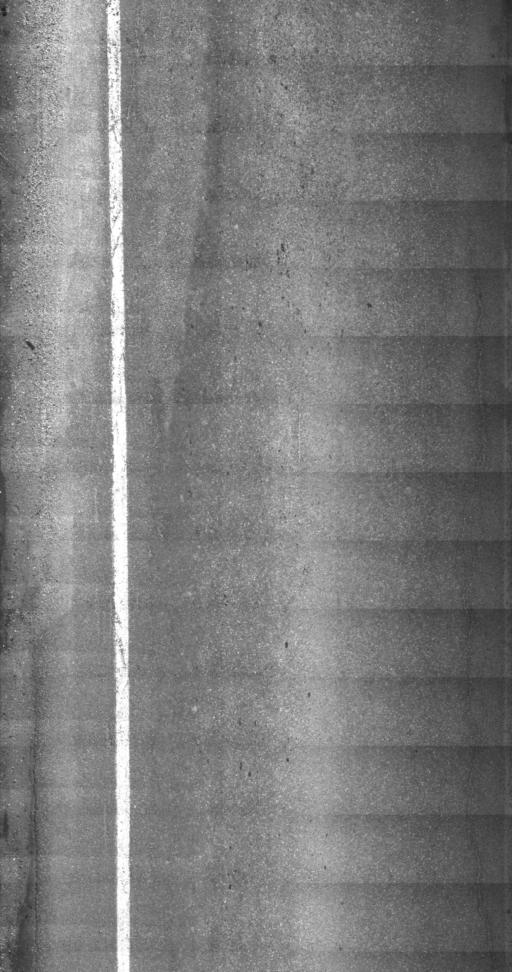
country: US
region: Vermont
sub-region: Chittenden County
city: Hinesburg
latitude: 44.3761
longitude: -73.1268
